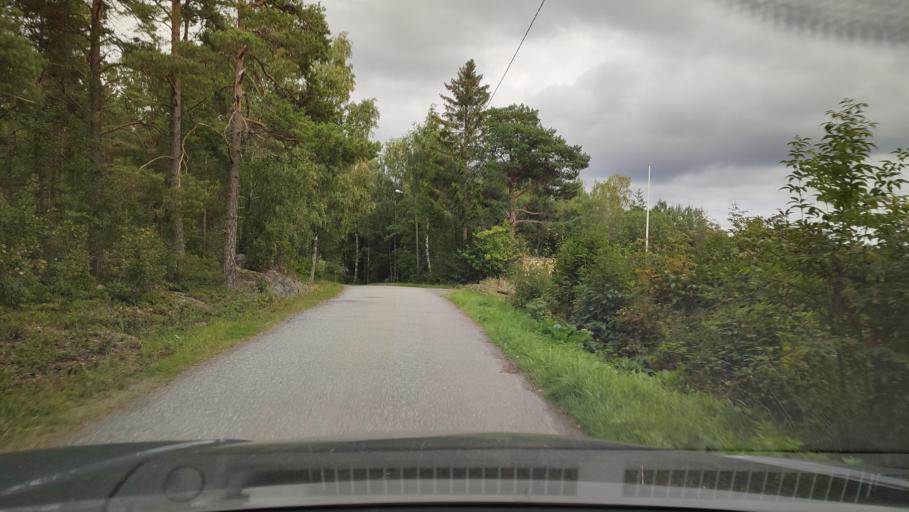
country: FI
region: Ostrobothnia
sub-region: Sydosterbotten
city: Kristinestad
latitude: 62.2487
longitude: 21.3336
